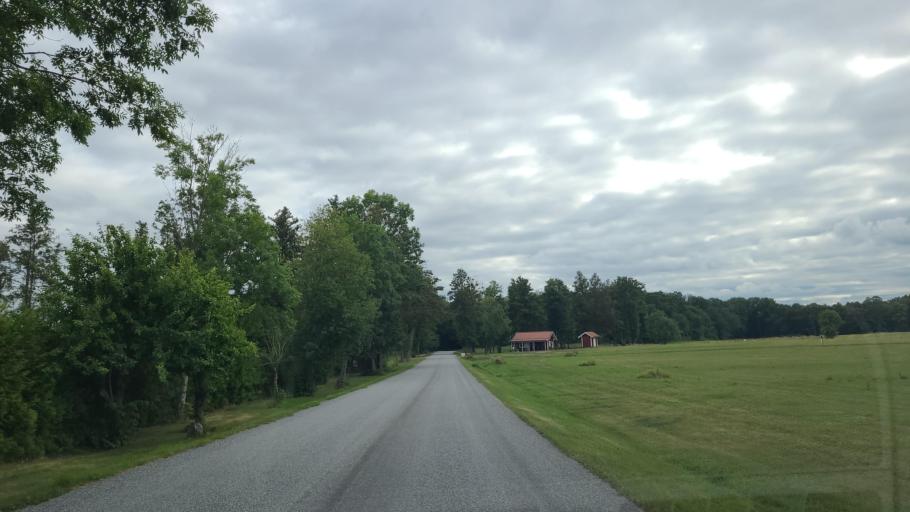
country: SE
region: Stockholm
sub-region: Upplands-Bro Kommun
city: Bro
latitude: 59.4845
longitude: 17.5687
